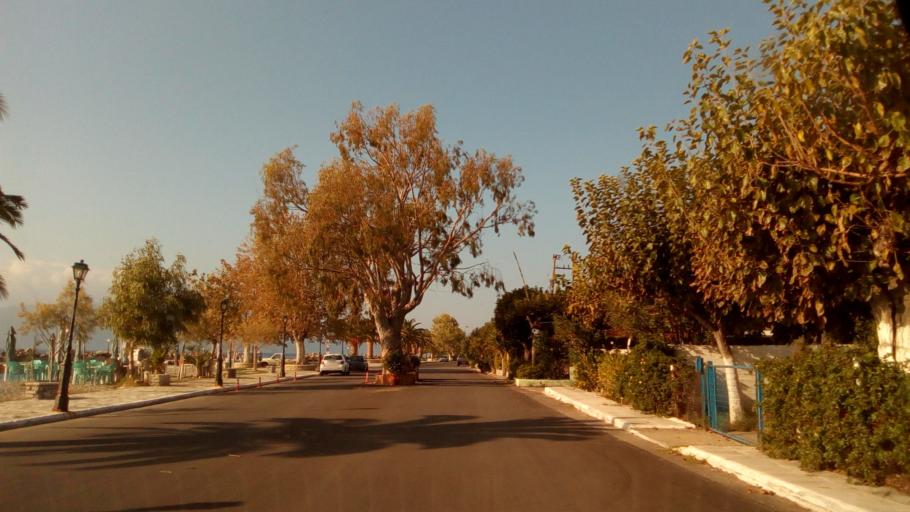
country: GR
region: West Greece
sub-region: Nomos Achaias
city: Kamarai
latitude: 38.3920
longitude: 22.0147
